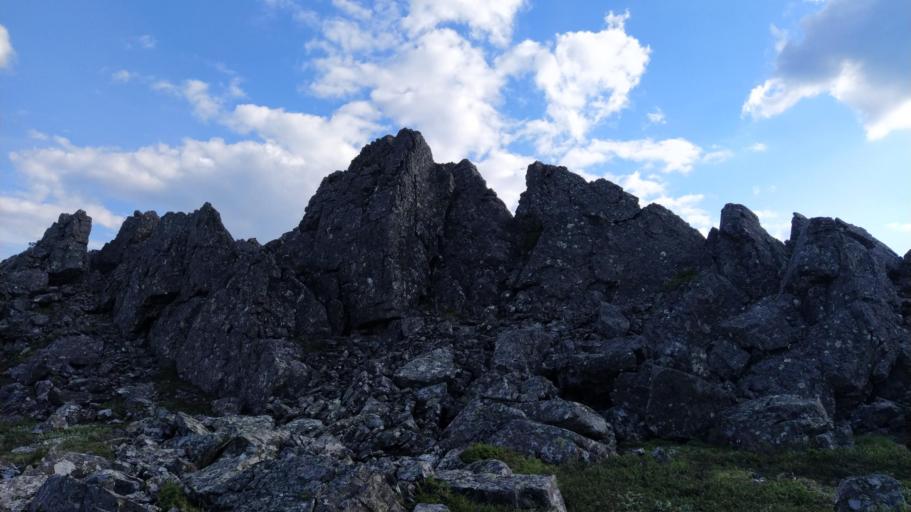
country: RU
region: Sverdlovsk
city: Karpinsk
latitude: 59.6058
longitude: 59.1728
